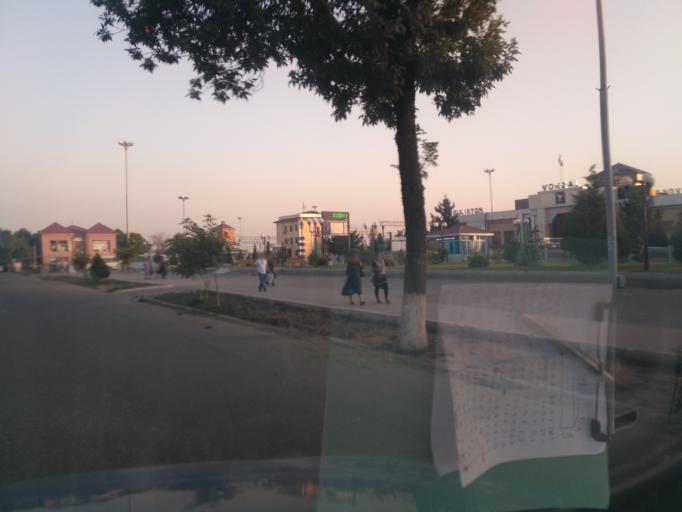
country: UZ
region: Sirdaryo
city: Guliston
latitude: 40.4969
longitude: 68.7659
